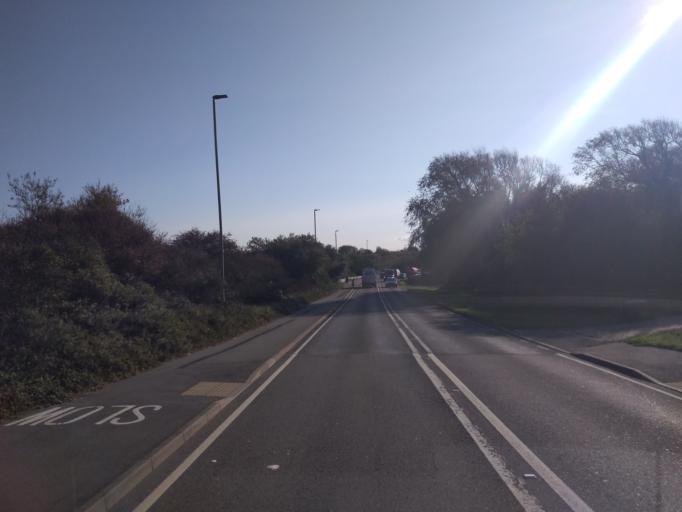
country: GB
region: England
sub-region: East Sussex
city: Newhaven
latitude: 50.7907
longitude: 0.0288
